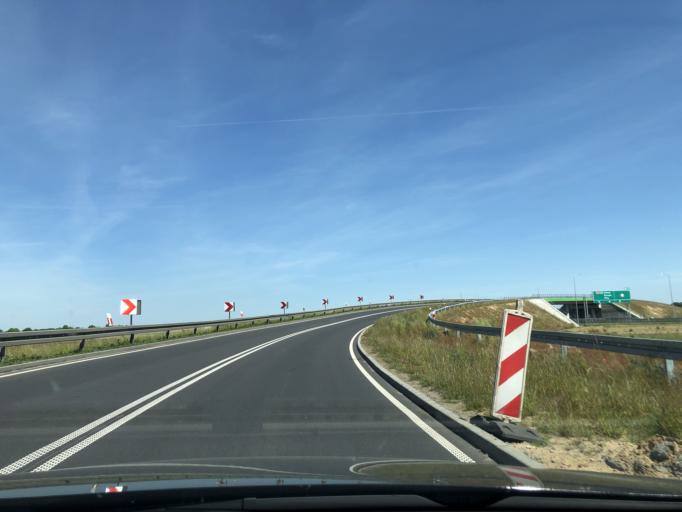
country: PL
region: West Pomeranian Voivodeship
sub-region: Powiat gryficki
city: Brojce
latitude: 53.8748
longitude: 15.3689
